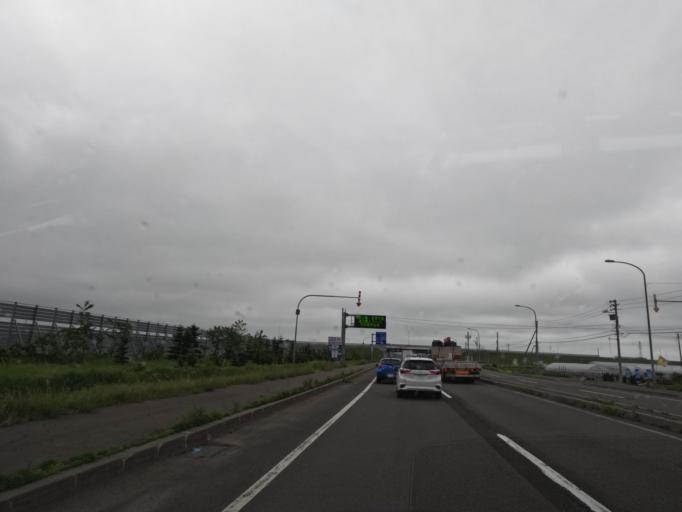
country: JP
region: Hokkaido
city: Tobetsu
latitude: 43.1811
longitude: 141.5229
